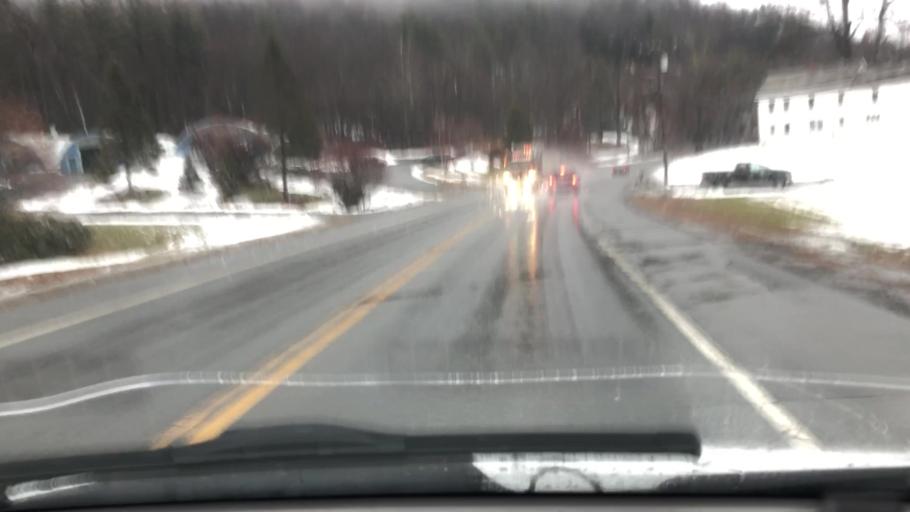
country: US
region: Massachusetts
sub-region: Franklin County
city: Shelburne Falls
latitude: 42.5914
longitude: -72.7207
